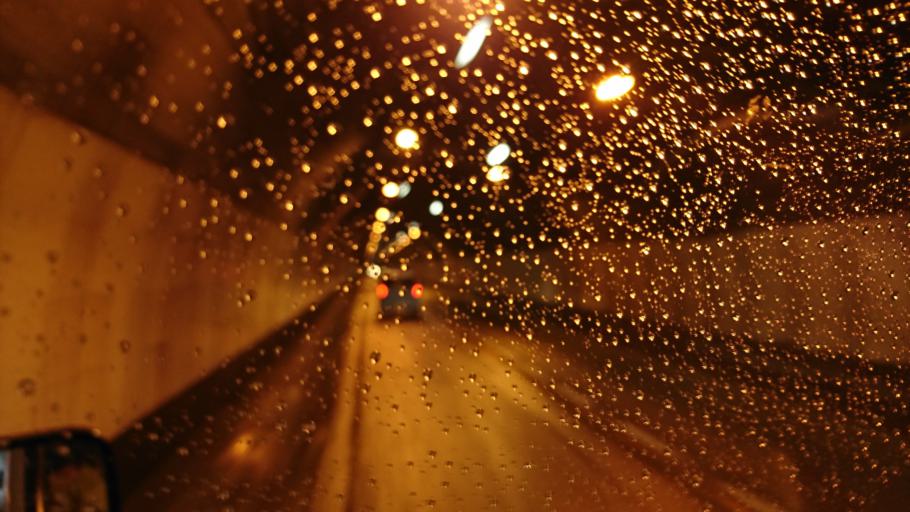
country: JP
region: Hyogo
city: Toyooka
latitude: 35.4816
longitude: 134.5841
